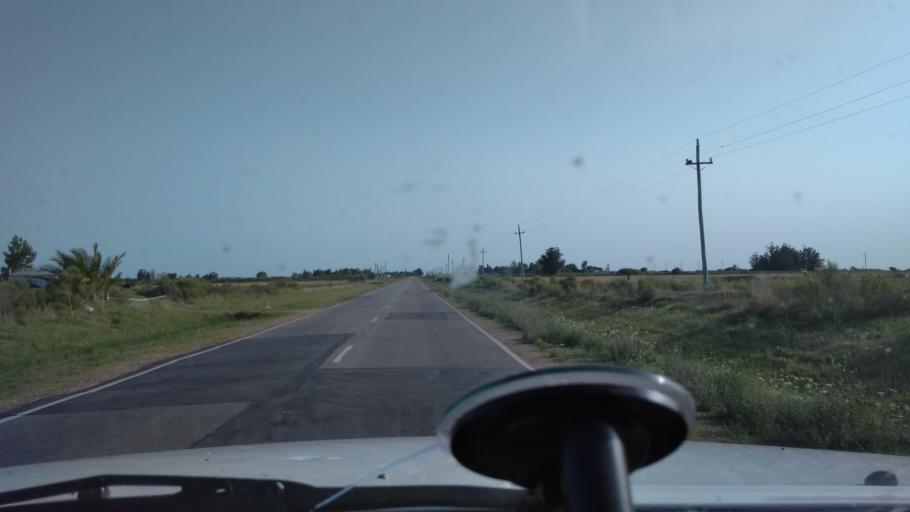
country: UY
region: Canelones
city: Santa Rosa
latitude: -34.5143
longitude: -56.0542
